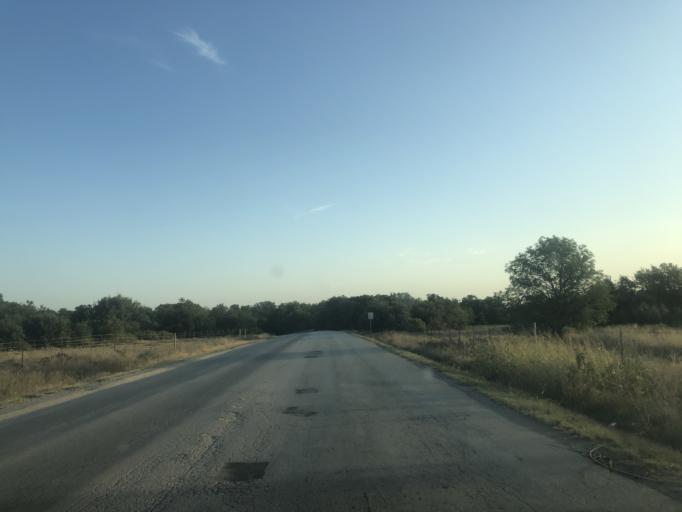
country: US
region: Texas
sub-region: Tarrant County
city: Lakeside
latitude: 32.7852
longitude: -97.4867
